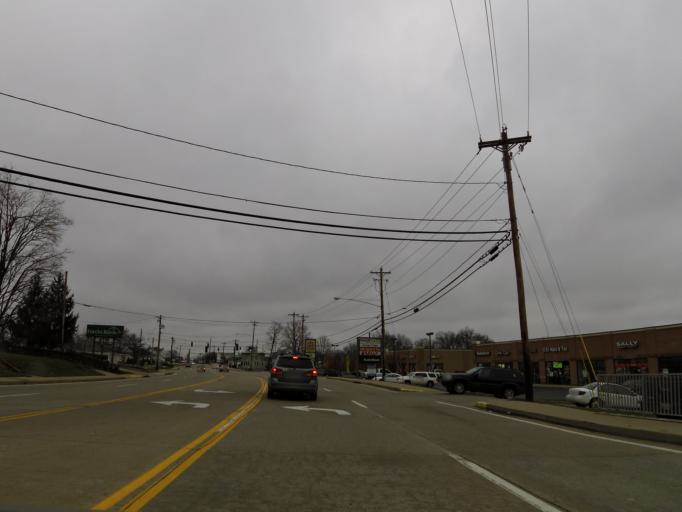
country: US
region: Kentucky
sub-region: Grant County
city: Dry Ridge
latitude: 38.6818
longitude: -84.5975
